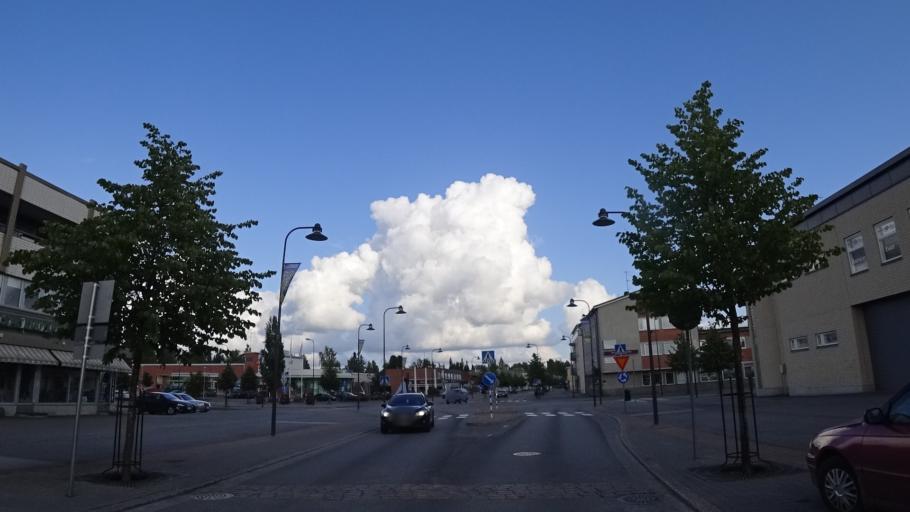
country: FI
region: North Karelia
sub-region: Pielisen Karjala
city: Lieksa
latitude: 63.3187
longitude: 30.0255
